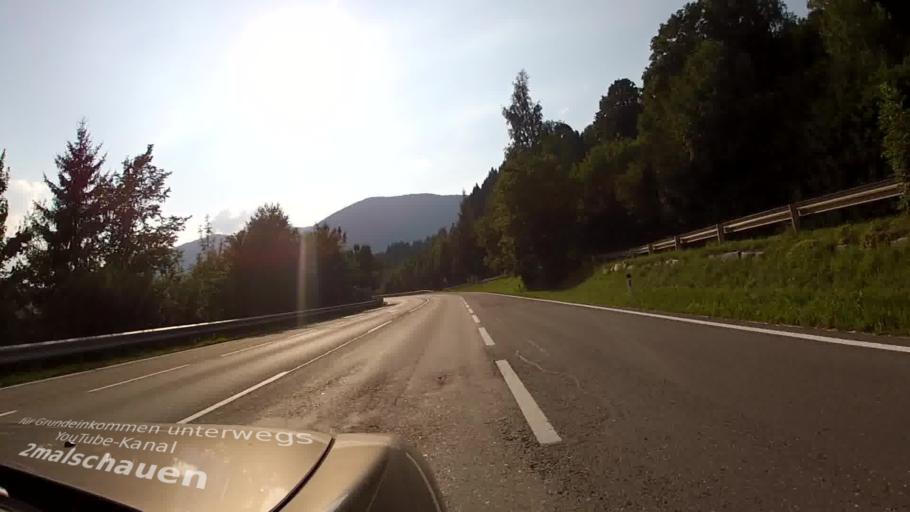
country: AT
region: Salzburg
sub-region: Politischer Bezirk Sankt Johann im Pongau
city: Altenmarkt im Pongau
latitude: 47.3847
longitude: 13.4271
